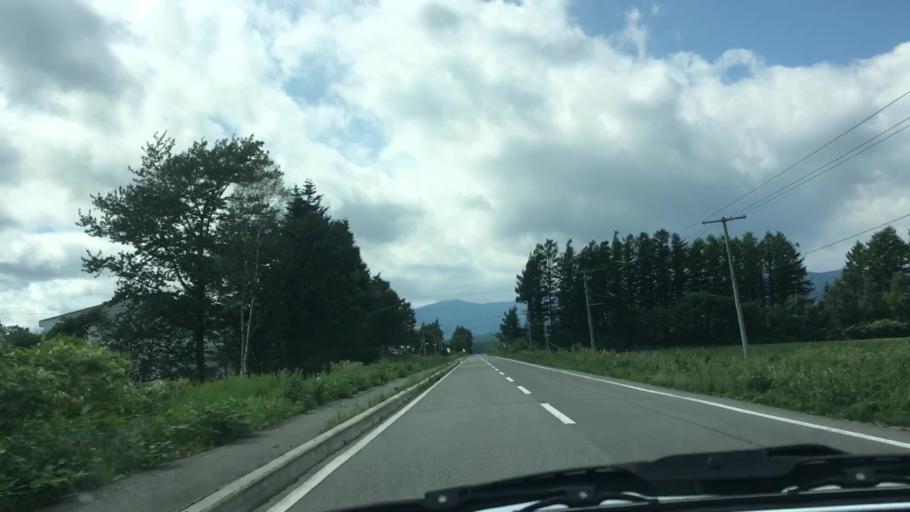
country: JP
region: Hokkaido
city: Otofuke
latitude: 43.2815
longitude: 143.3297
